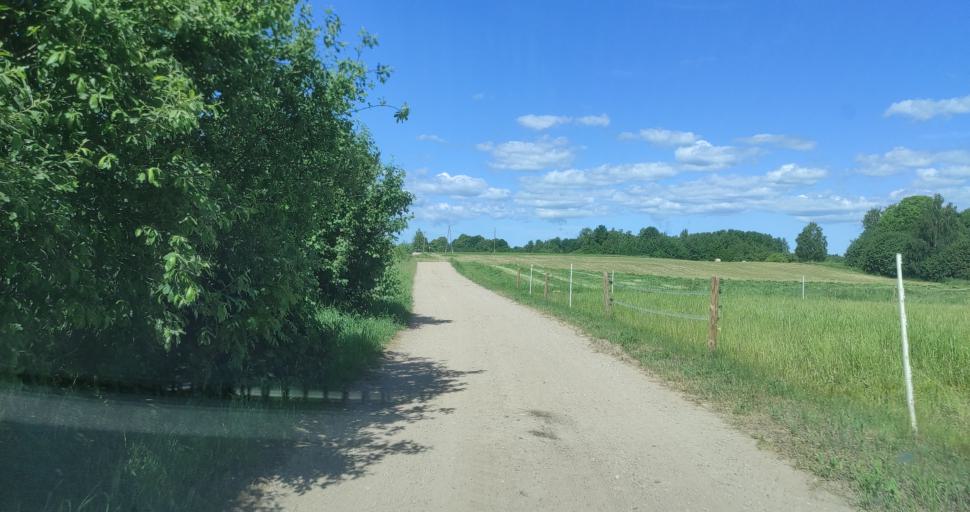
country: LV
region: Alsunga
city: Alsunga
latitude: 56.8983
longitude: 21.7121
